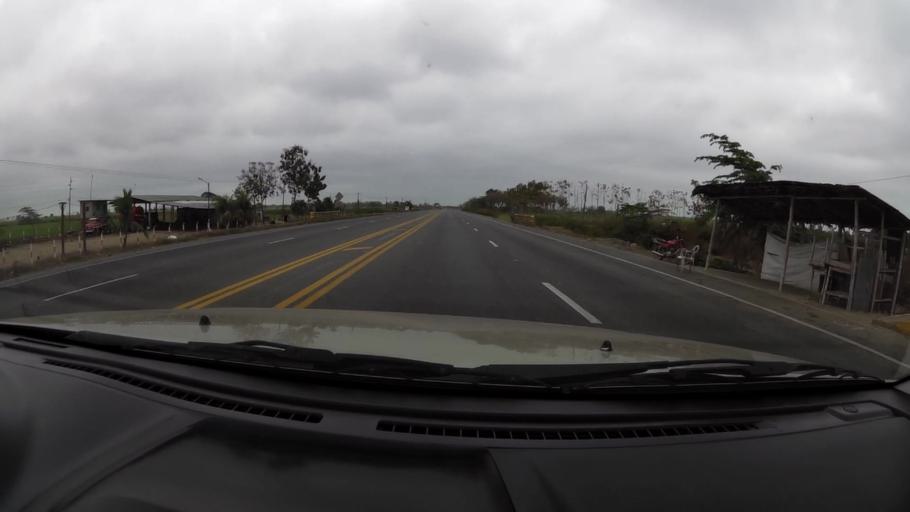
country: EC
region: Guayas
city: Naranjal
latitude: -2.4731
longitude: -79.6207
